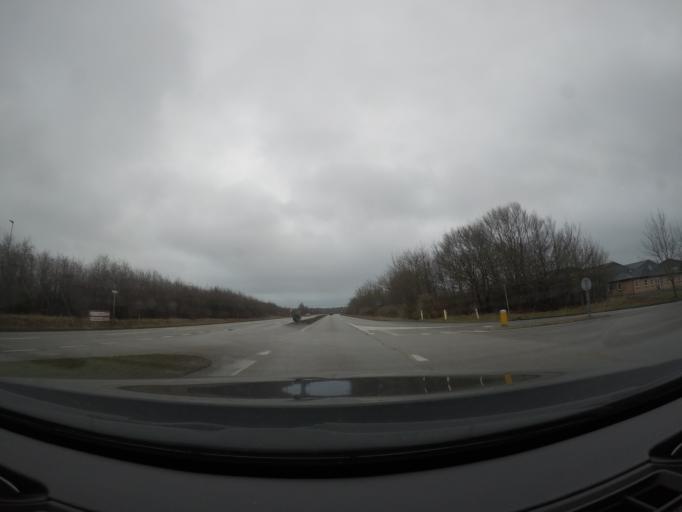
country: DK
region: South Denmark
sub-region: Kolding Kommune
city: Kolding
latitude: 55.5488
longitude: 9.5074
